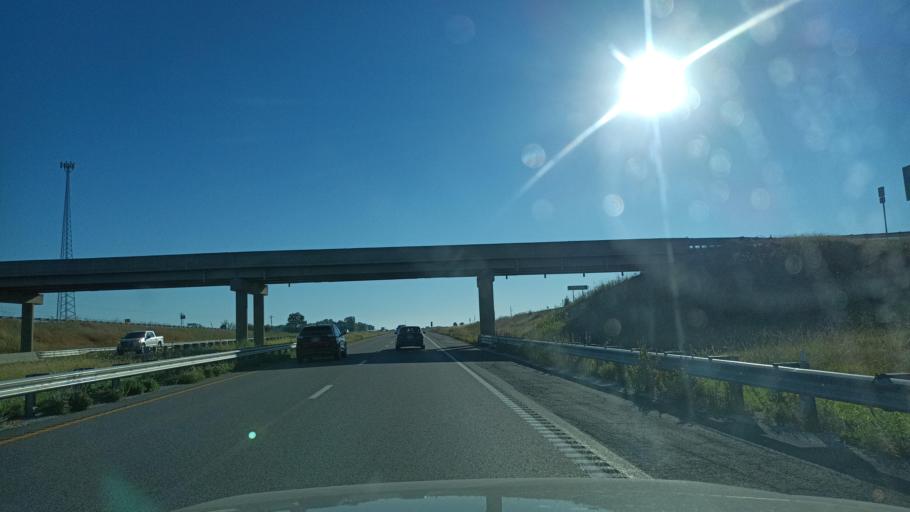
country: US
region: Missouri
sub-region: Callaway County
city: Fulton
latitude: 38.9520
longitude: -92.0094
